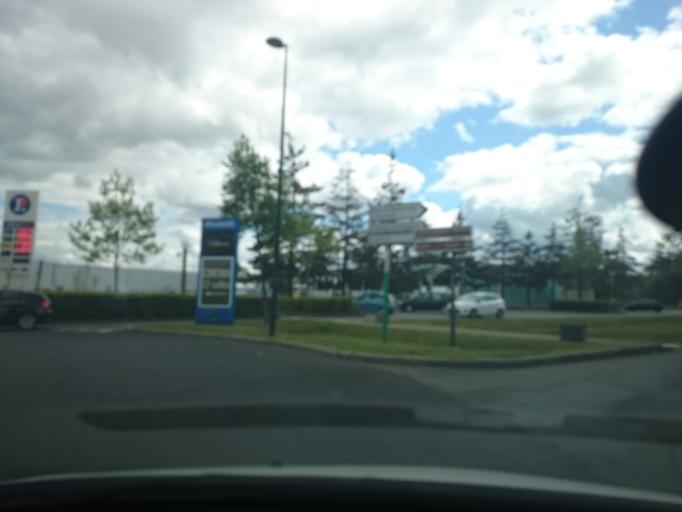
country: FR
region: Pays de la Loire
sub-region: Departement de la Loire-Atlantique
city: Saint-Herblain
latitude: 47.2266
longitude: -1.6348
